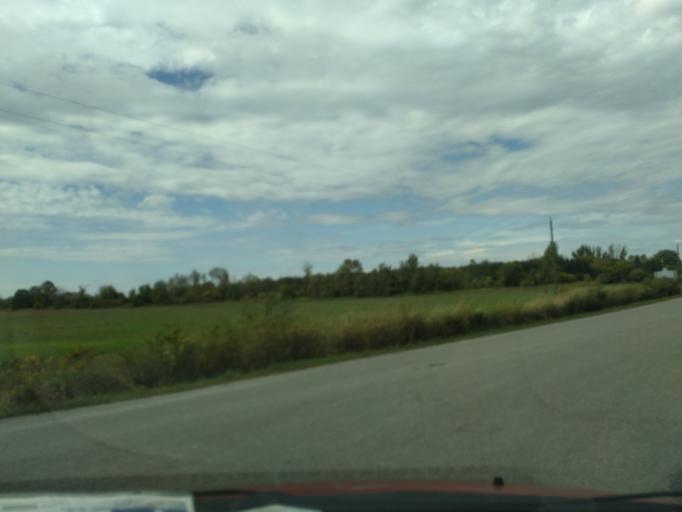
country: CA
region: Ontario
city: Keswick
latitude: 44.2629
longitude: -79.3645
